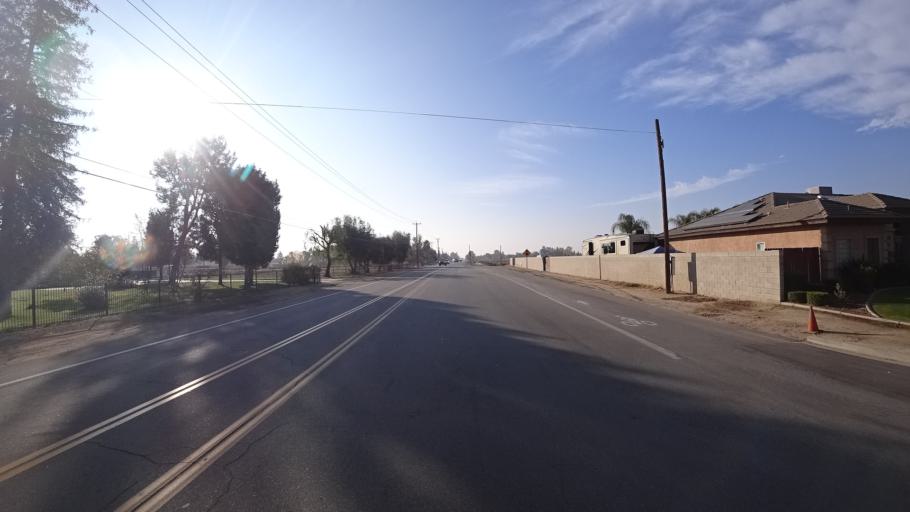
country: US
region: California
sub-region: Kern County
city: Rosedale
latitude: 35.3710
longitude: -119.1634
